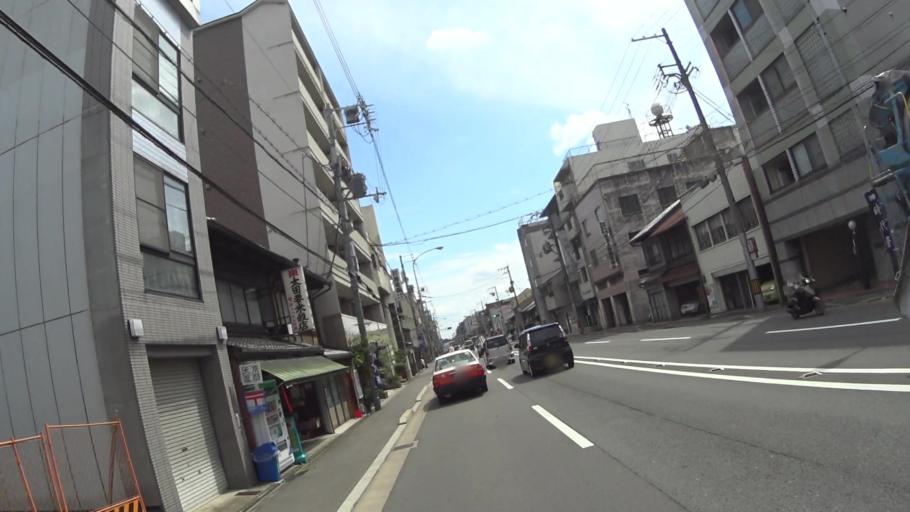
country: JP
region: Kyoto
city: Kyoto
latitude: 34.9951
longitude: 135.7492
